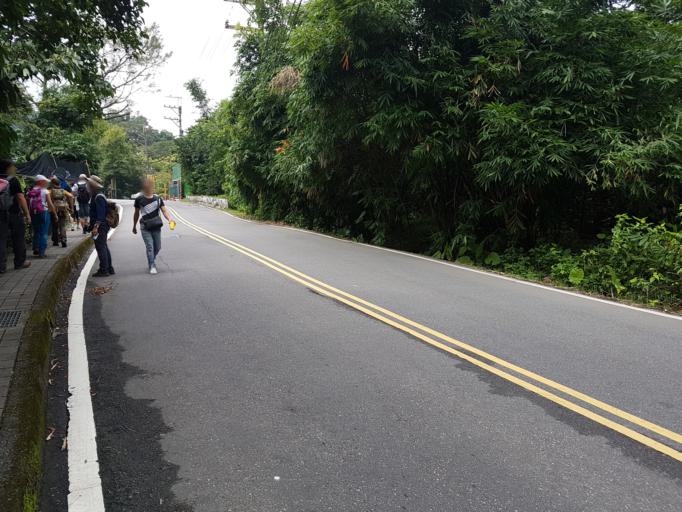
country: TW
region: Taiwan
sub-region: Keelung
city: Keelung
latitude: 25.0603
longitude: 121.6596
